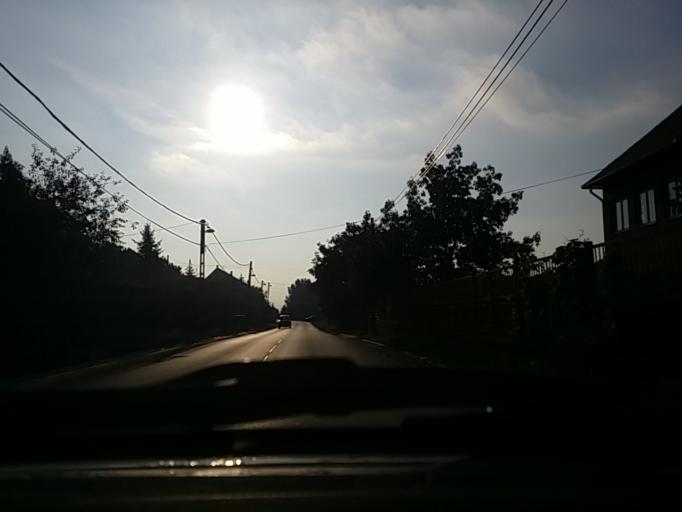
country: HU
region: Pest
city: Szentendre
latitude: 47.6832
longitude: 19.0454
